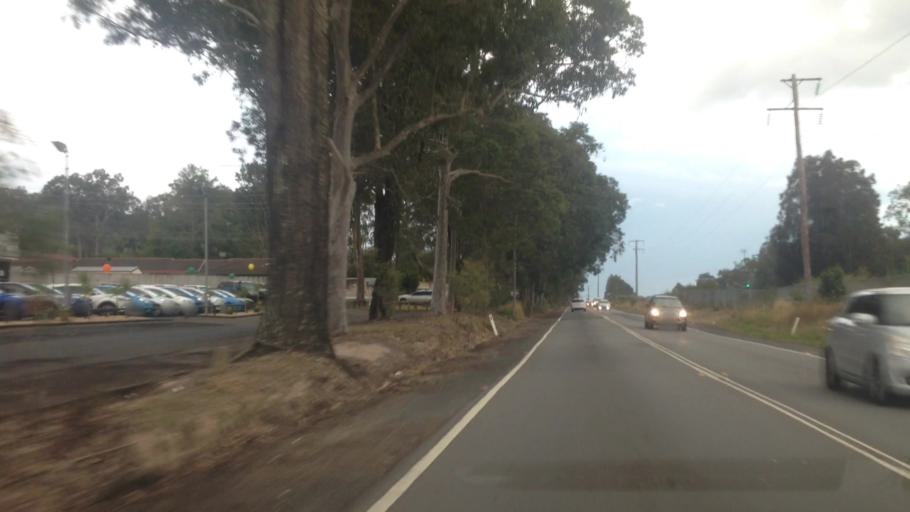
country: AU
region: New South Wales
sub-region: Wyong Shire
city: Jilliby
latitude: -33.2736
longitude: 151.4299
